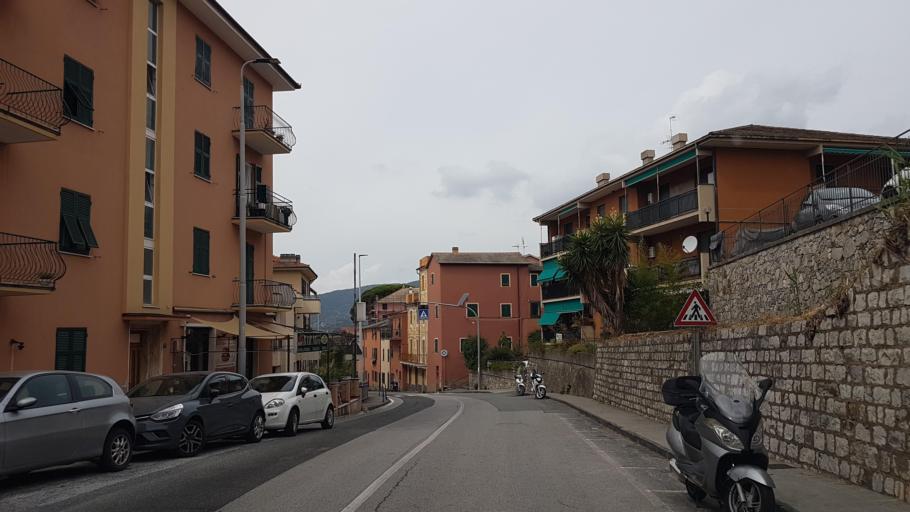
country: IT
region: Liguria
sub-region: Provincia di Genova
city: Casarza Ligure
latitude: 44.2648
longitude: 9.4295
